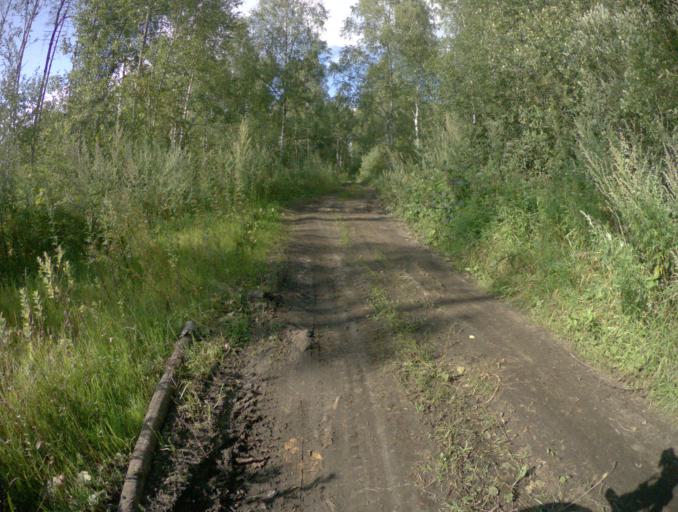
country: RU
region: Vladimir
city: Sobinka
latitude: 55.9439
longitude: 40.0585
